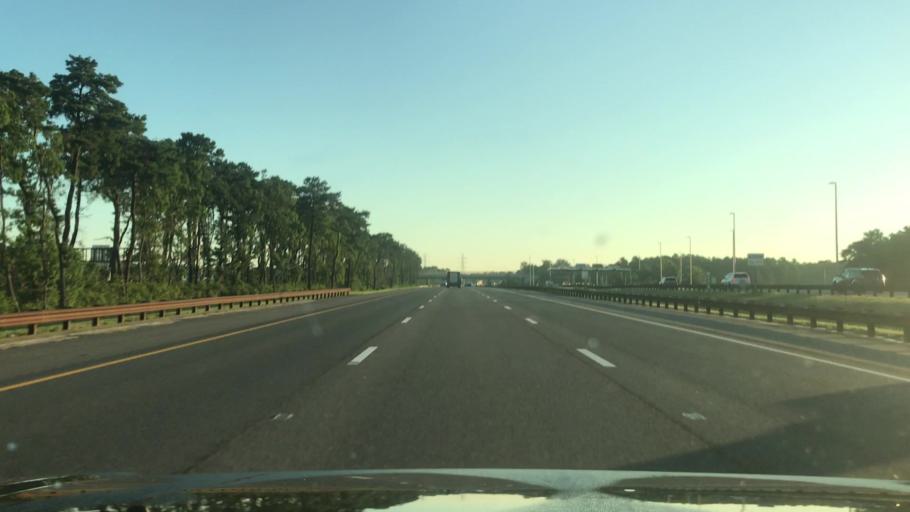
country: US
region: New Jersey
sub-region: Ocean County
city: Leisure Village
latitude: 40.0612
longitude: -74.1641
